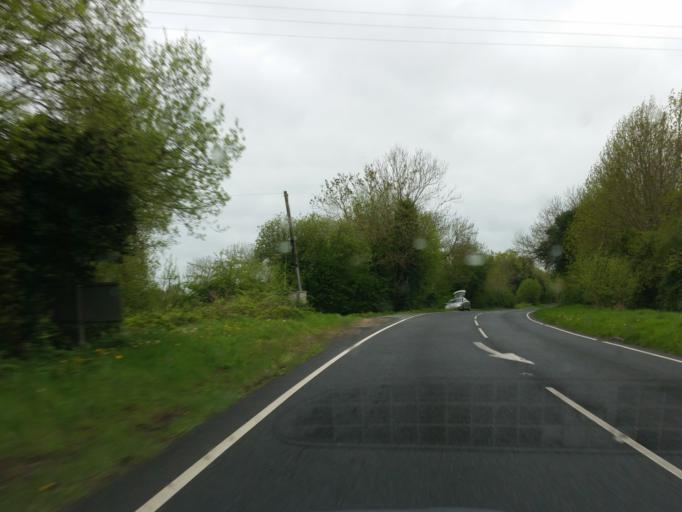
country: GB
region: Northern Ireland
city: Lisnaskea
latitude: 54.2115
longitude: -7.4755
